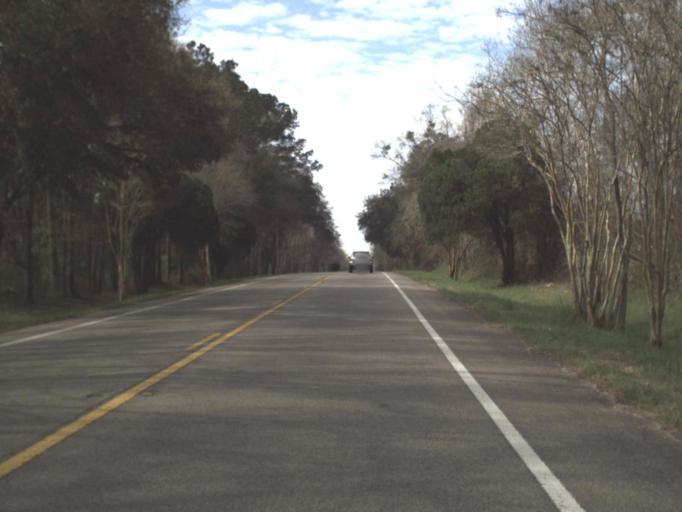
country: US
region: Florida
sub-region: Leon County
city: Tallahassee
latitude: 30.5012
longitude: -84.0989
